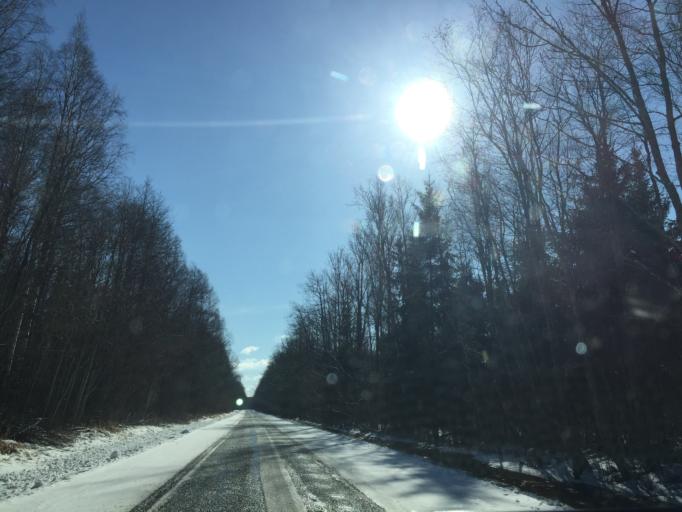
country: LV
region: Salacgrivas
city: Ainazi
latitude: 58.0021
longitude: 24.5182
